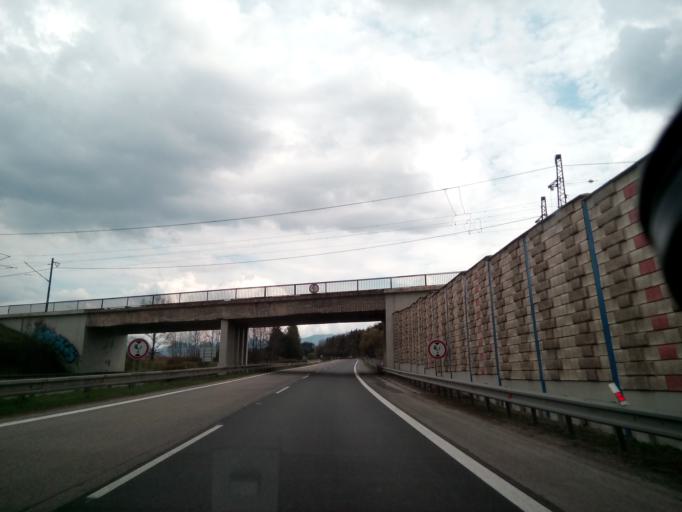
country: SK
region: Zilinsky
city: Ruzomberok
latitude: 49.0954
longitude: 19.4432
